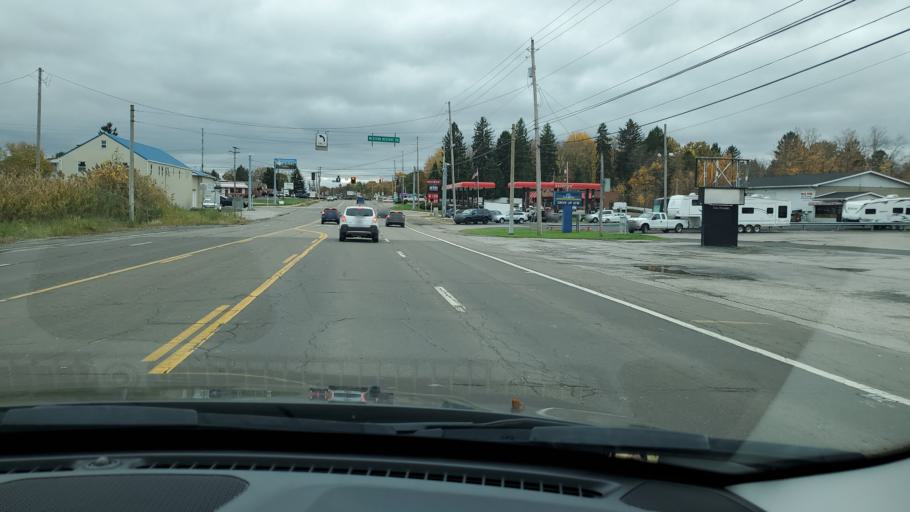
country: US
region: Ohio
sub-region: Mahoning County
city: Boardman
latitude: 40.9892
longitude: -80.6628
